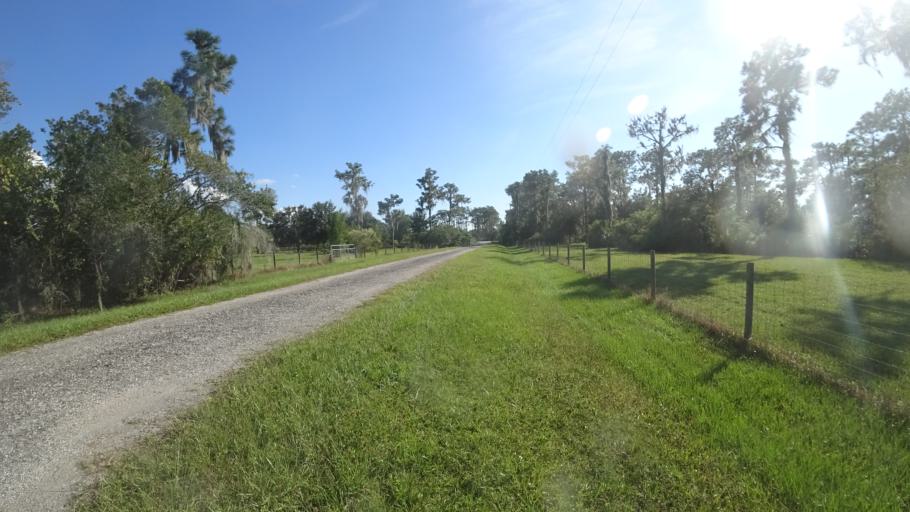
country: US
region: Florida
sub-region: Sarasota County
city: Lake Sarasota
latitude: 27.3948
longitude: -82.2917
